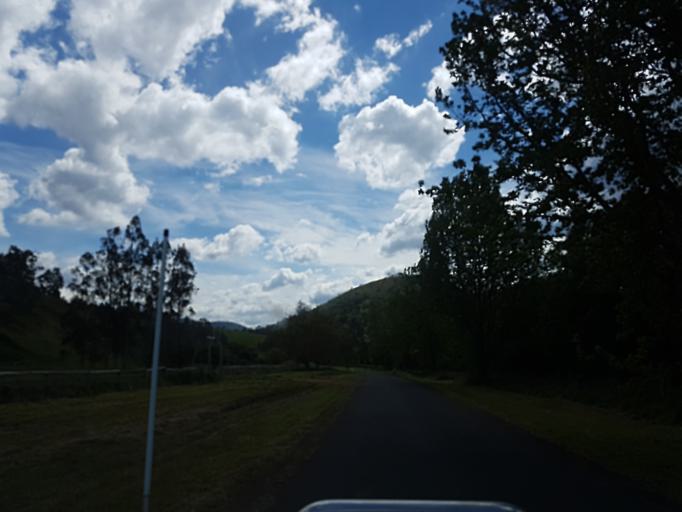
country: AU
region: Victoria
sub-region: East Gippsland
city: Bairnsdale
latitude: -37.4416
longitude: 147.2505
